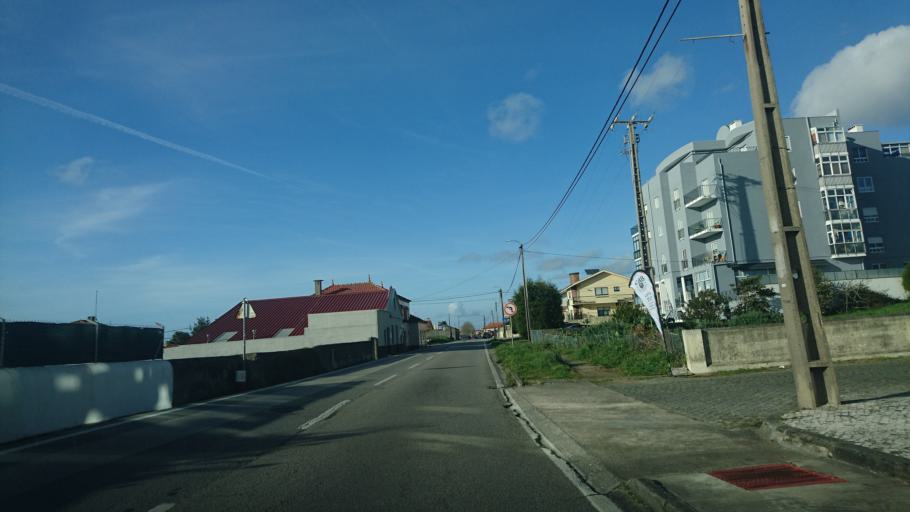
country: PT
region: Aveiro
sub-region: Ovar
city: Esmoriz
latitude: 40.9637
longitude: -8.6288
